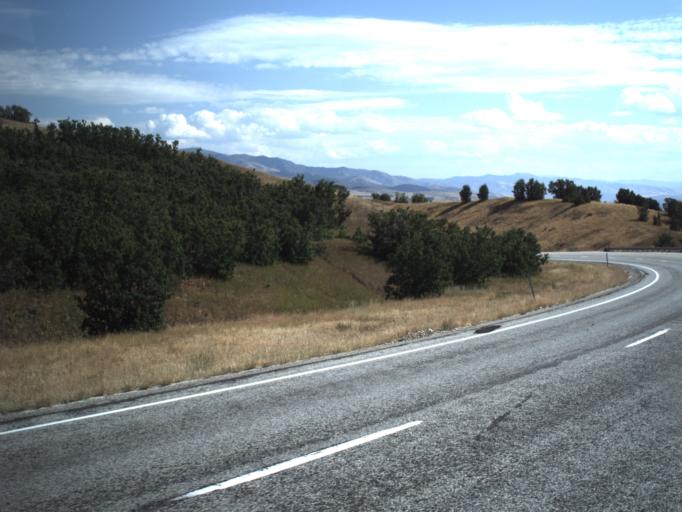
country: US
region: Utah
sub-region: Morgan County
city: Mountain Green
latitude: 41.1703
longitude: -111.8122
